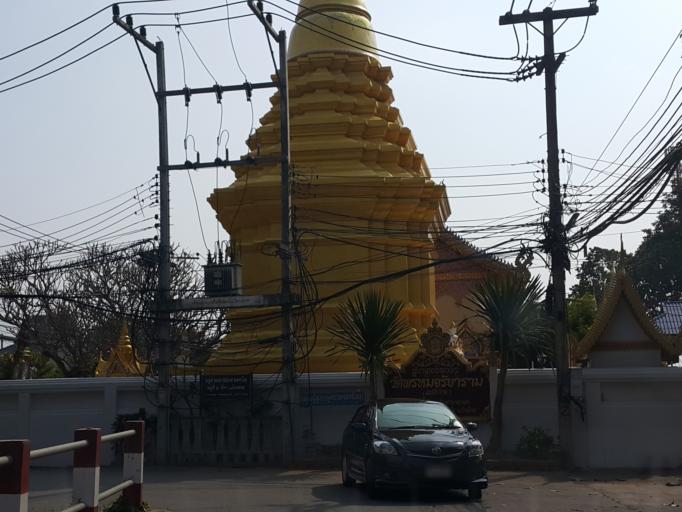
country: TH
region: Chiang Mai
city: San Kamphaeng
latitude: 18.8113
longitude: 99.1215
